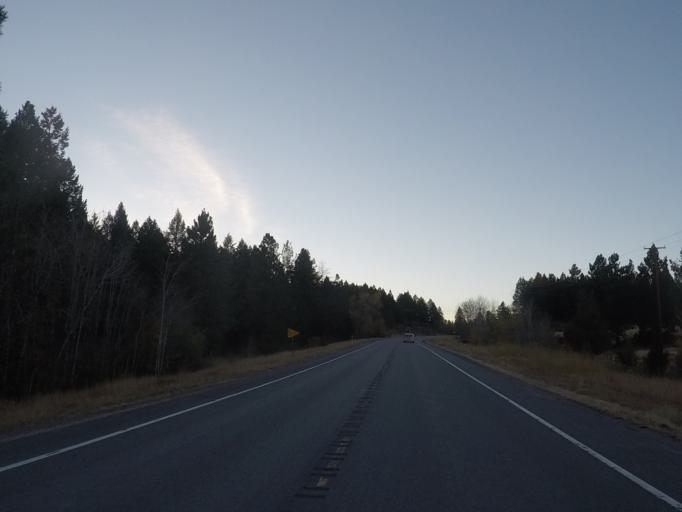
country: US
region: Montana
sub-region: Lewis and Clark County
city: Lincoln
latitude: 47.0081
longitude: -113.0541
